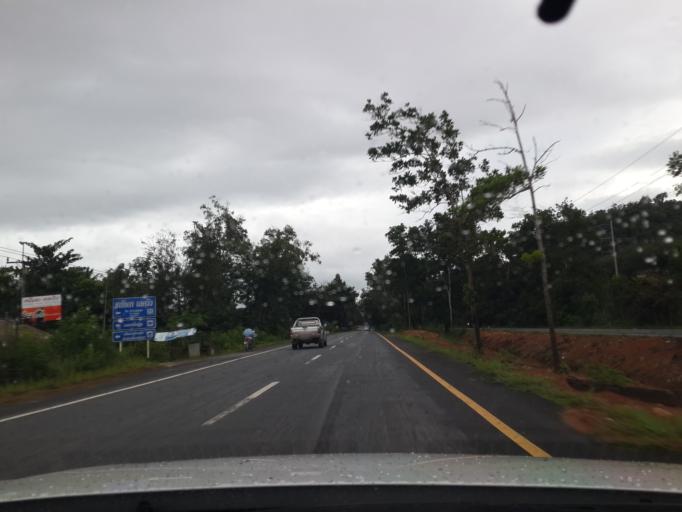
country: TH
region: Songkhla
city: Na Mom
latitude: 6.9615
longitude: 100.5280
